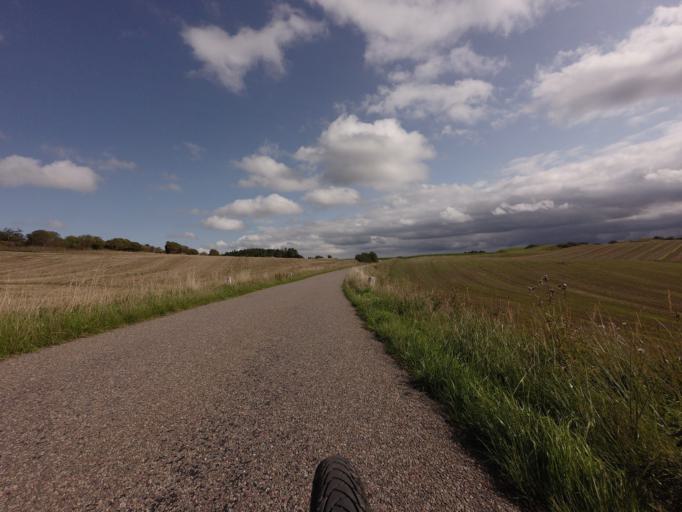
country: DK
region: North Denmark
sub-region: Hjorring Kommune
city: Hjorring
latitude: 57.5296
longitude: 10.0422
